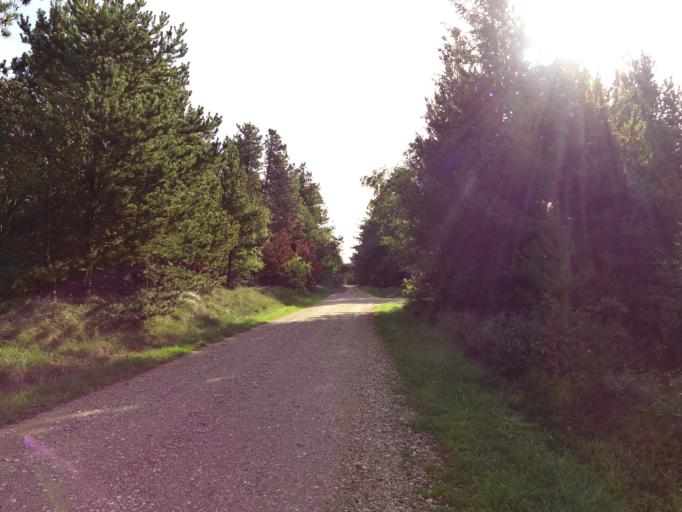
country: DK
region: South Denmark
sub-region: Varde Kommune
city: Oksbol
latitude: 55.5592
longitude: 8.2143
